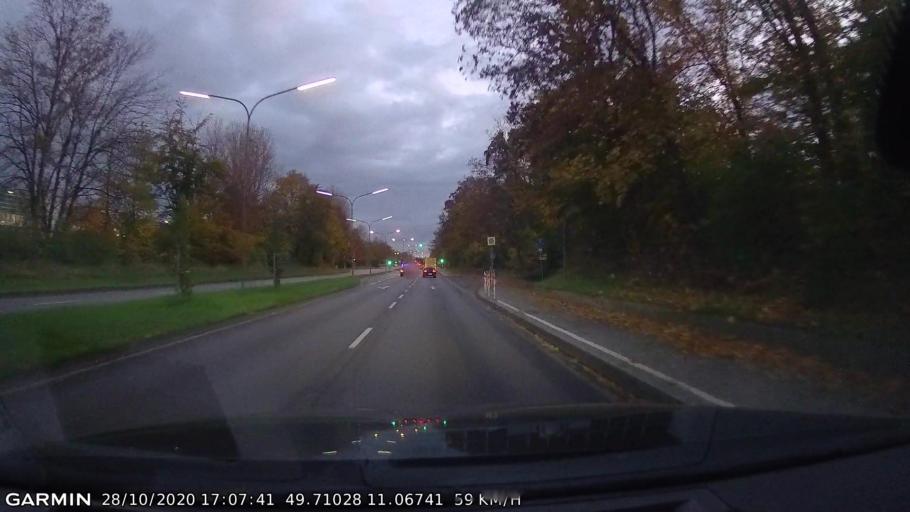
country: DE
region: Bavaria
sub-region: Upper Franconia
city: Forchheim
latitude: 49.7102
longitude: 11.0674
